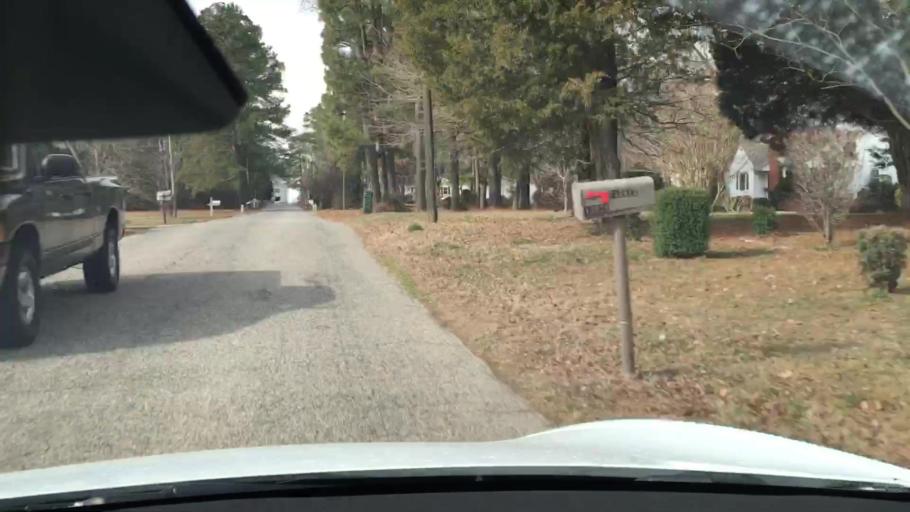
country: US
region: Virginia
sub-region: Chesterfield County
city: Brandermill
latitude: 37.5085
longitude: -77.6589
